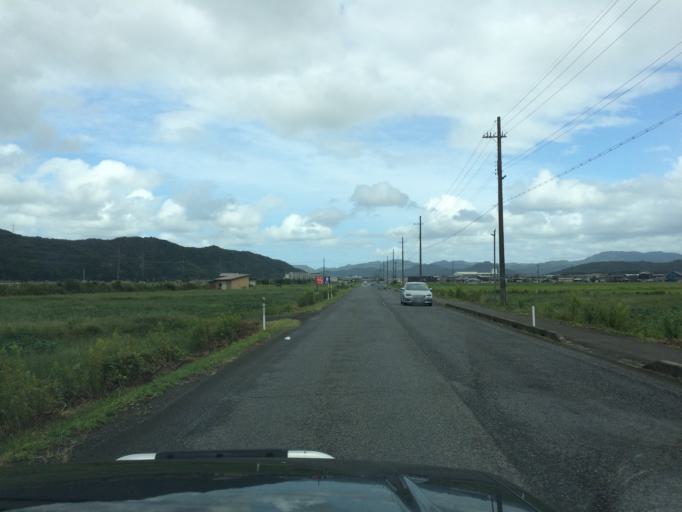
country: JP
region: Hyogo
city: Toyooka
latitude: 35.4853
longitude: 134.7915
